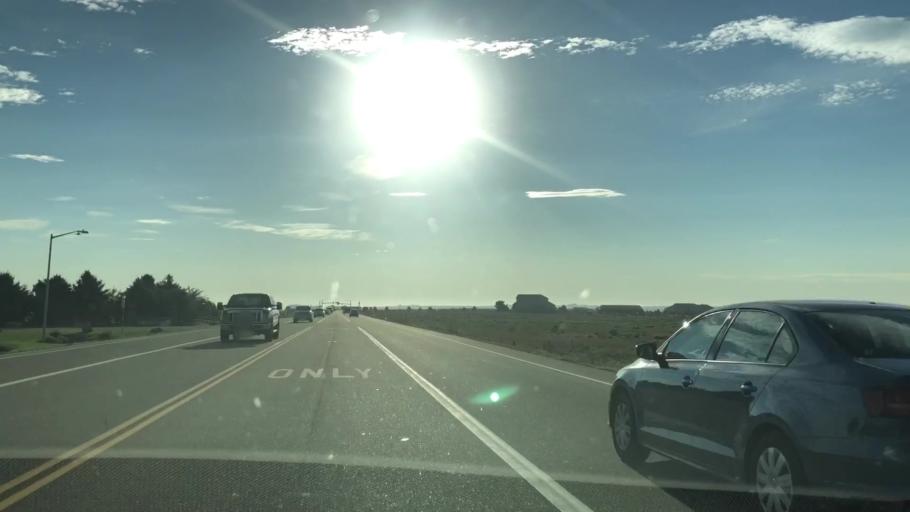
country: US
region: Colorado
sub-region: Weld County
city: Windsor
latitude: 40.4359
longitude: -104.9522
